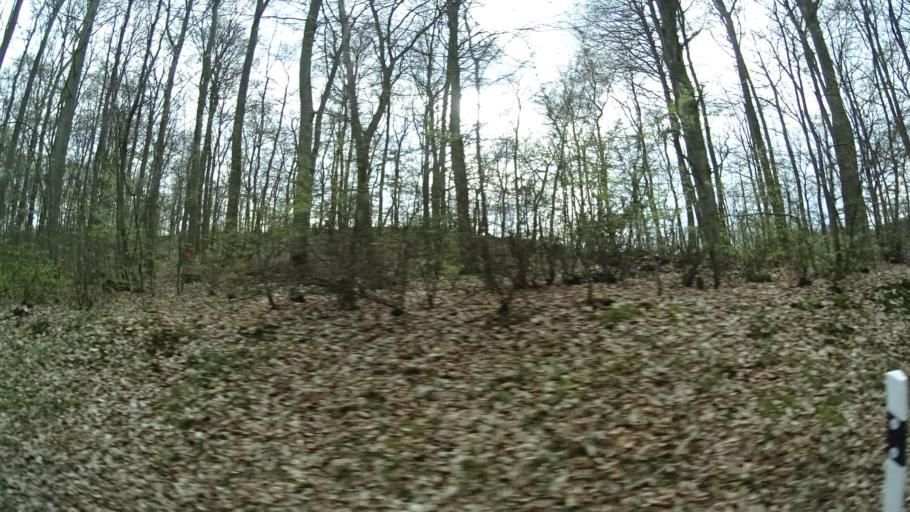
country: DE
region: Rheinland-Pfalz
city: Bockenau
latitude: 49.8267
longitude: 7.6660
